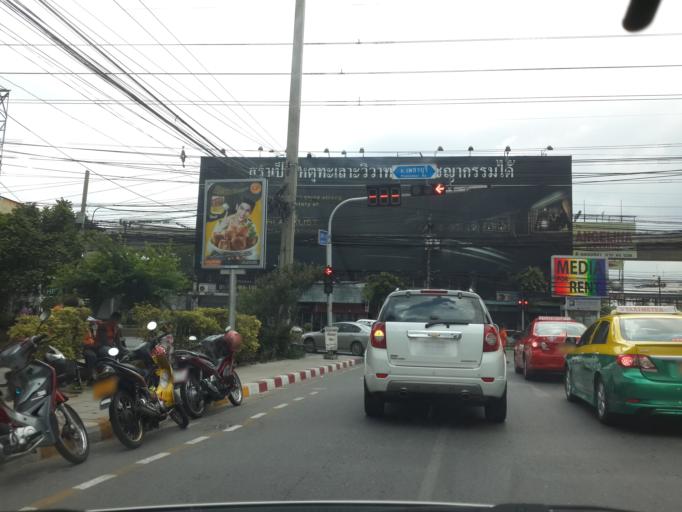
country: TH
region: Bangkok
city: Watthana
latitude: 13.7441
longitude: 100.5860
